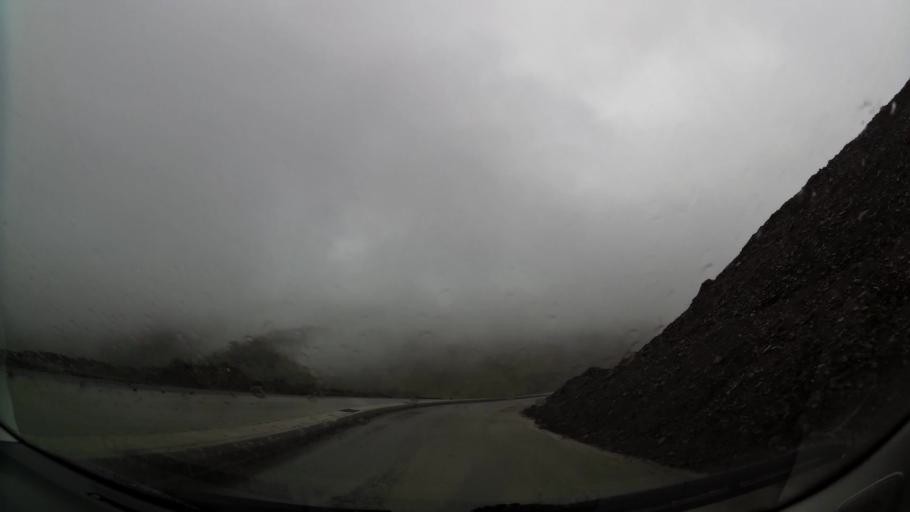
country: MA
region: Taza-Al Hoceima-Taounate
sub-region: Taza
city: Aknoul
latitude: 34.7765
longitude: -3.7909
